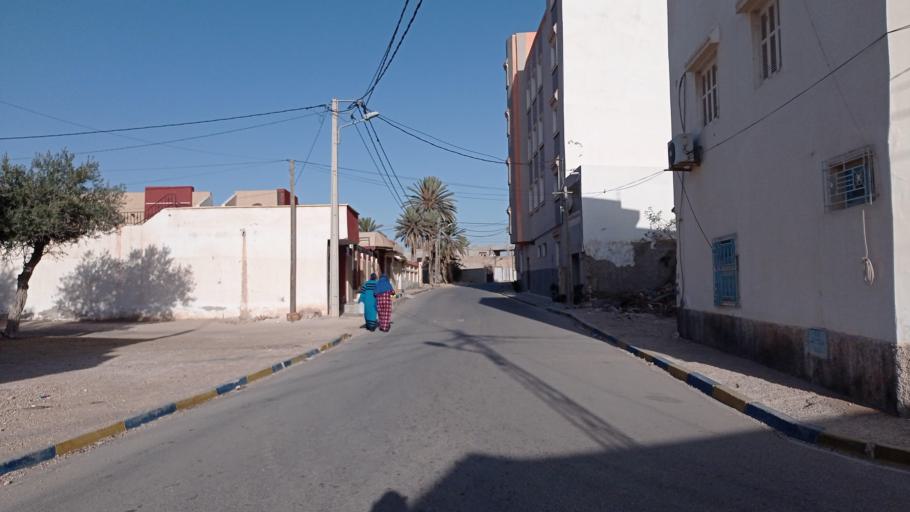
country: TN
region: Qabis
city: Gabes
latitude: 33.8576
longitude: 10.1181
